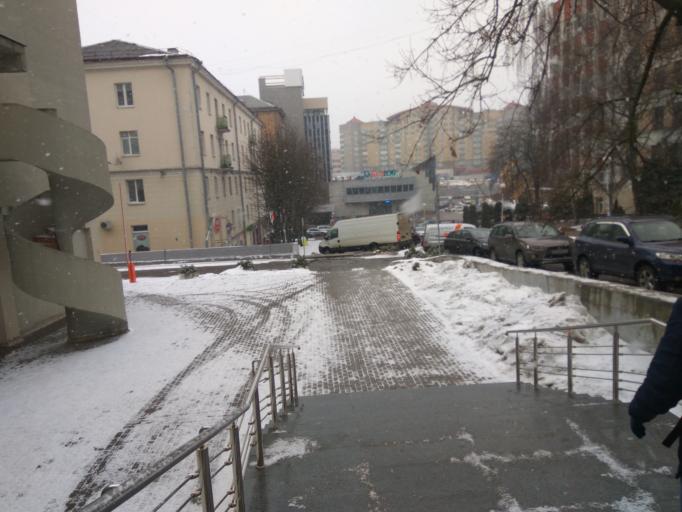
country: BY
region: Minsk
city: Minsk
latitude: 53.8975
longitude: 27.5452
